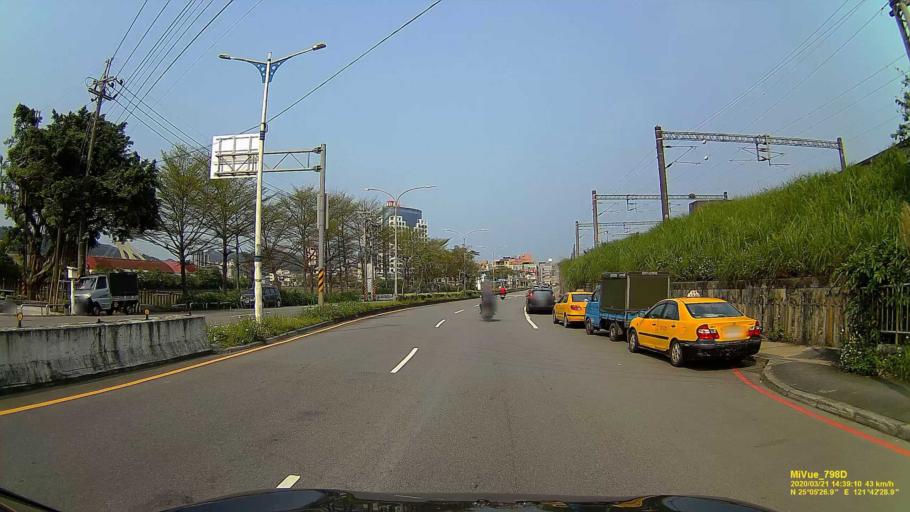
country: TW
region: Taiwan
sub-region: Keelung
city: Keelung
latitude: 25.0903
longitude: 121.7081
